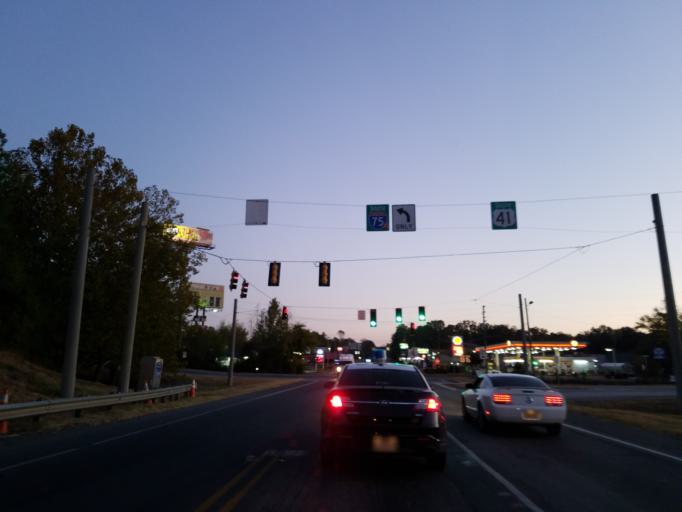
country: US
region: Georgia
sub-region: Gordon County
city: Calhoun
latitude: 34.5564
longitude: -84.9359
